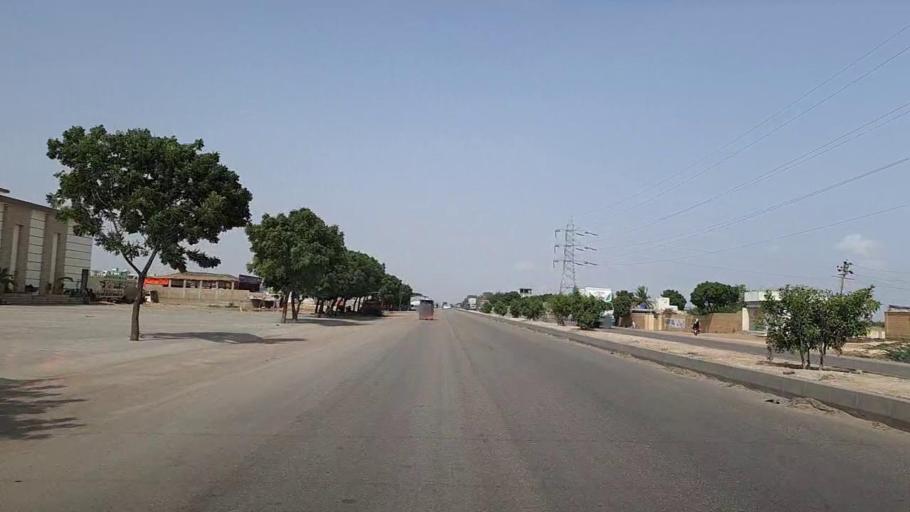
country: PK
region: Sindh
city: Malir Cantonment
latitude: 24.8625
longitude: 67.3544
